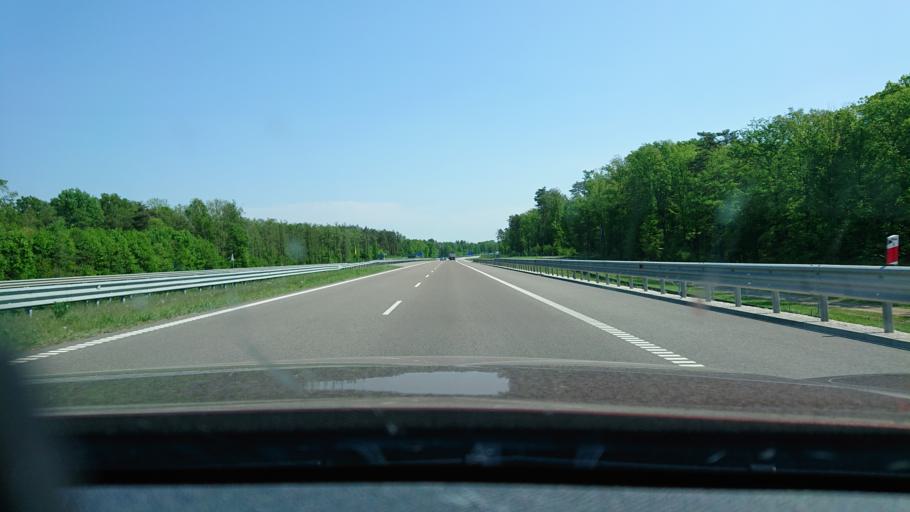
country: PL
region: Subcarpathian Voivodeship
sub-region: Powiat przemyski
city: Stubno
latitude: 49.9582
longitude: 23.0500
